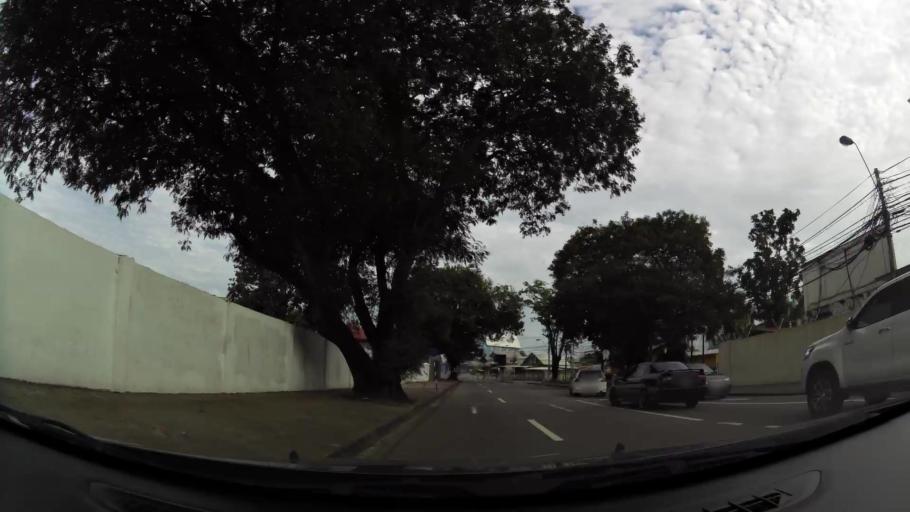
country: TT
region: City of Port of Spain
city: Port-of-Spain
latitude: 10.6571
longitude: -61.5172
